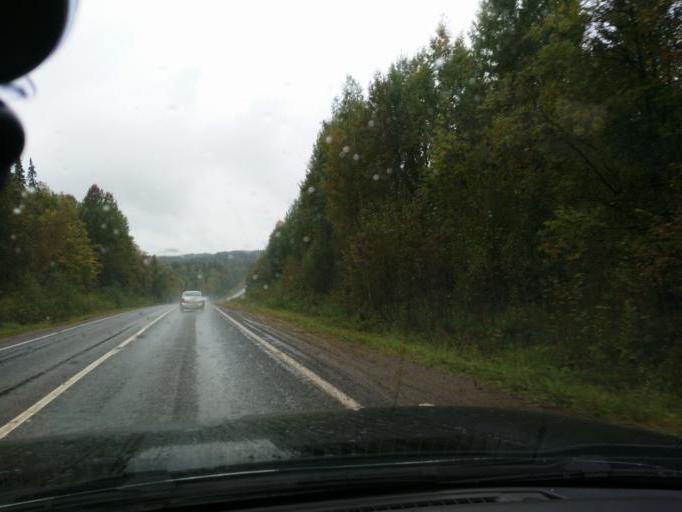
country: RU
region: Perm
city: Yugo-Kamskiy
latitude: 57.6120
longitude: 55.6372
